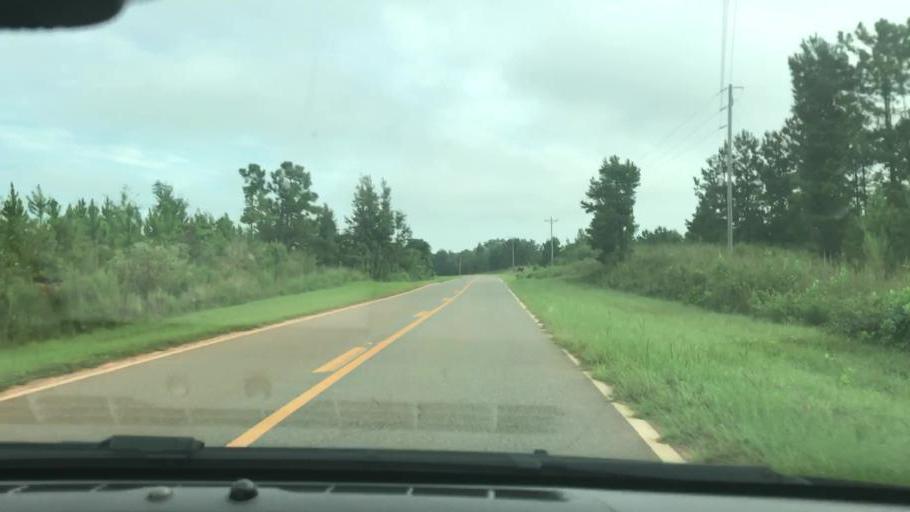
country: US
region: Georgia
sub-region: Stewart County
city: Lumpkin
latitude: 32.0360
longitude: -84.9101
